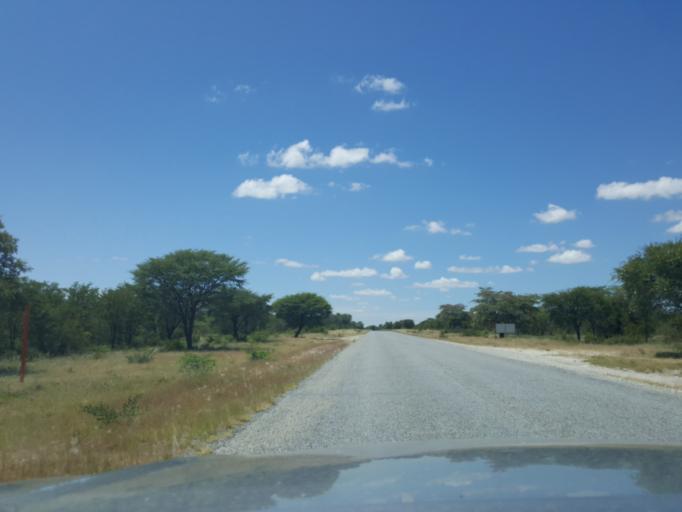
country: BW
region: Central
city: Nata
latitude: -20.1473
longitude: 25.7292
